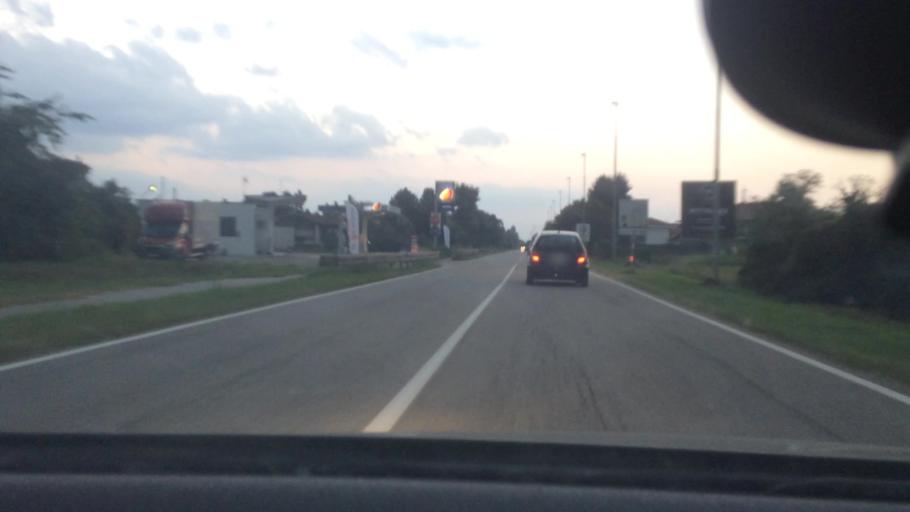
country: IT
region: Lombardy
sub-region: Citta metropolitana di Milano
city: Buscate
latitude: 45.5453
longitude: 8.8011
